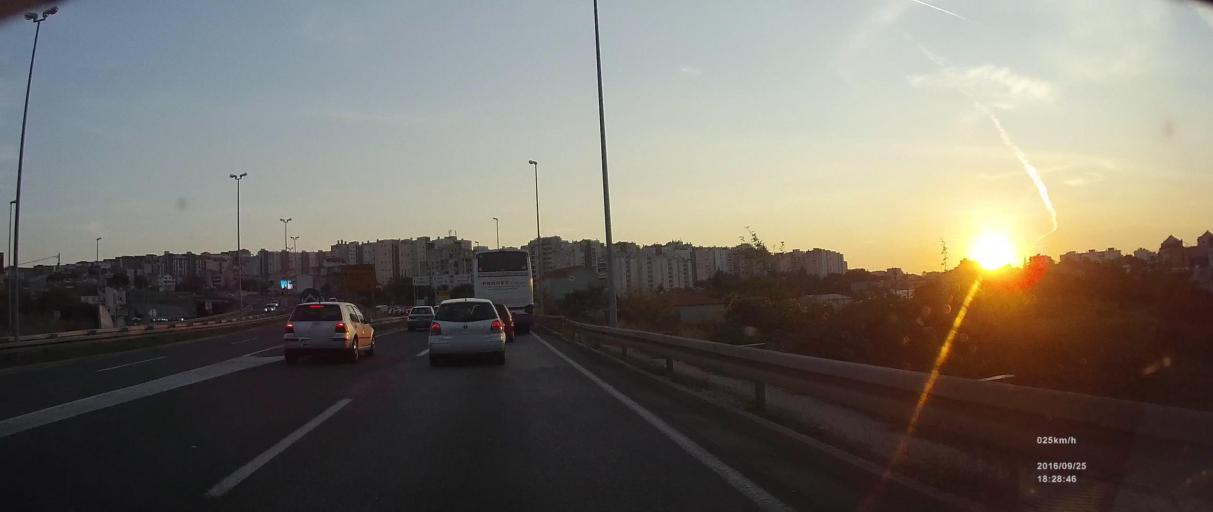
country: HR
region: Splitsko-Dalmatinska
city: Vranjic
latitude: 43.5204
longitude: 16.4826
